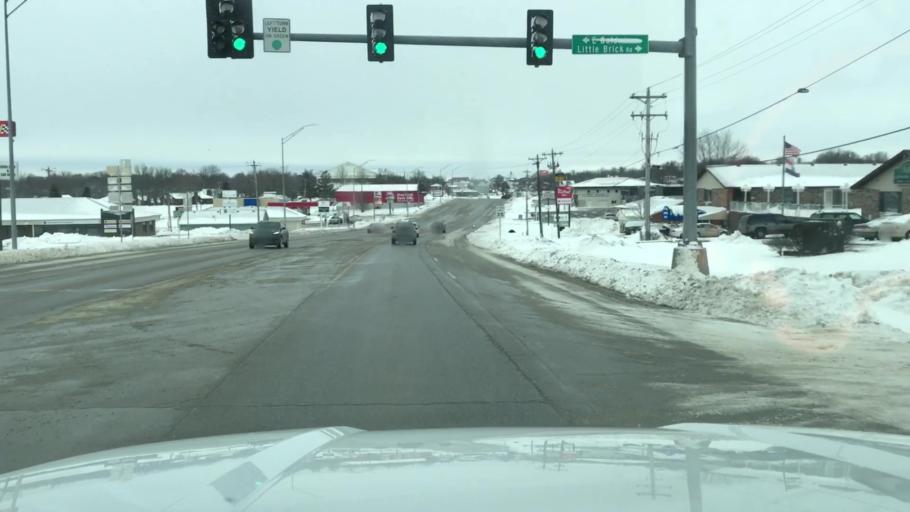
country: US
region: Missouri
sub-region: Clinton County
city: Cameron
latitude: 39.7529
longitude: -94.2344
